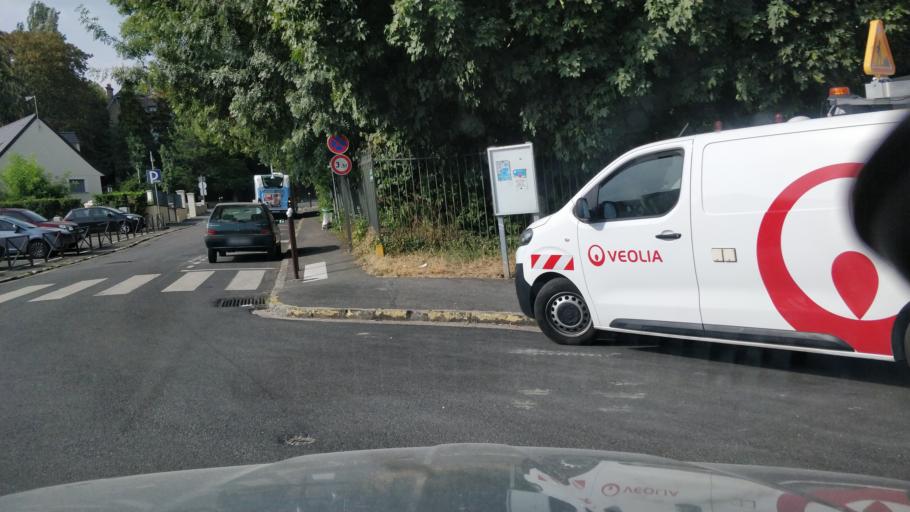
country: FR
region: Ile-de-France
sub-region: Departement de Seine-et-Marne
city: Thorigny-sur-Marne
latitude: 48.8822
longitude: 2.7011
